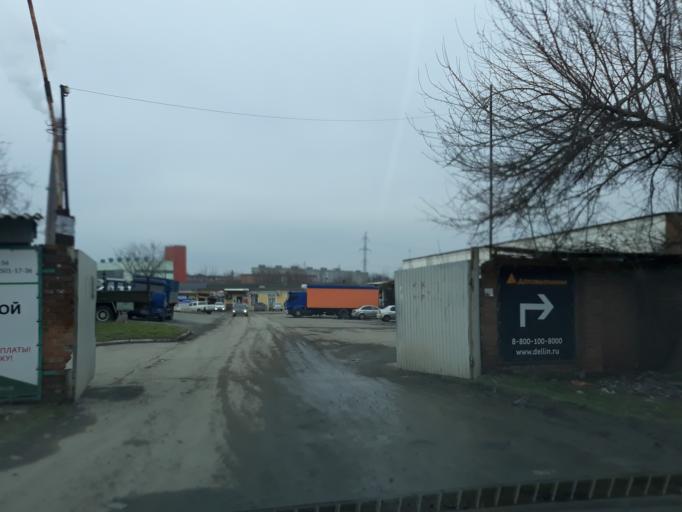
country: RU
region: Rostov
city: Taganrog
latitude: 47.2166
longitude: 38.8775
